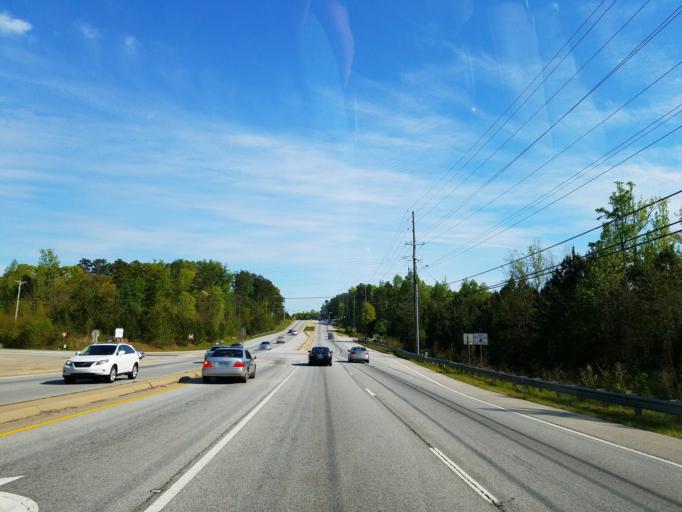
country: US
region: Georgia
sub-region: Douglas County
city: Lithia Springs
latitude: 33.7077
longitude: -84.6613
